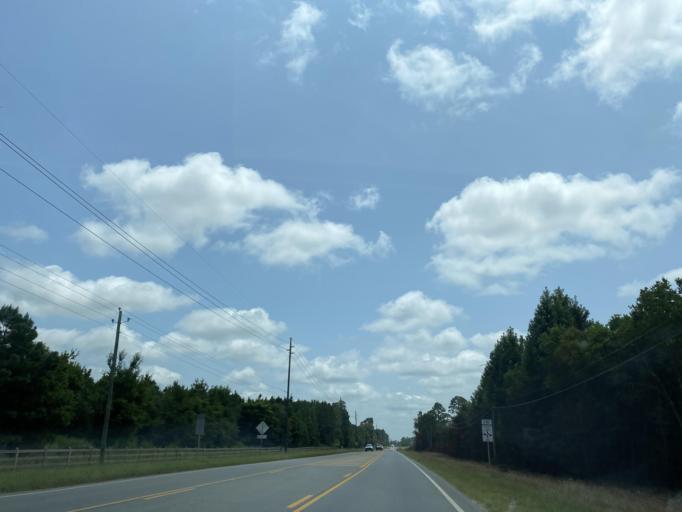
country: US
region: Georgia
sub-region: Jeff Davis County
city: Hazlehurst
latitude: 31.8386
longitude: -82.5815
